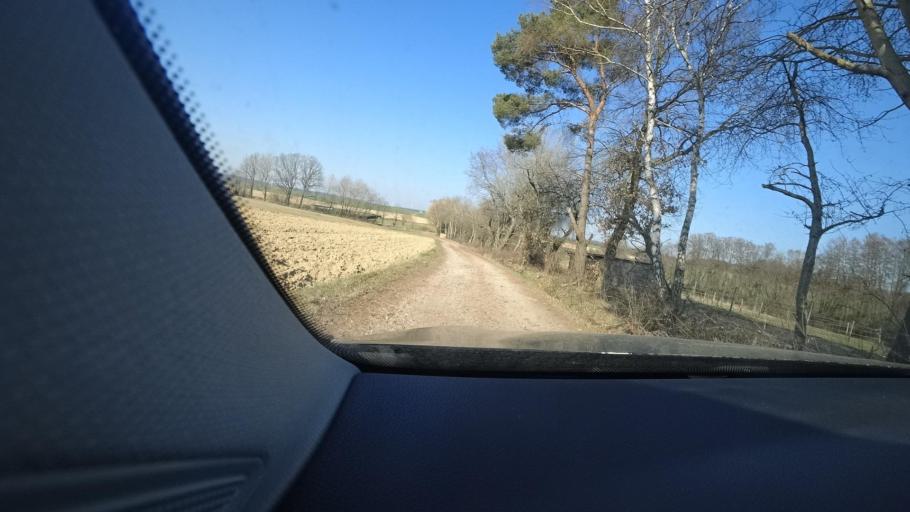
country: DE
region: Rheinland-Pfalz
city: Morschbach
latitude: 50.0016
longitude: 7.6201
